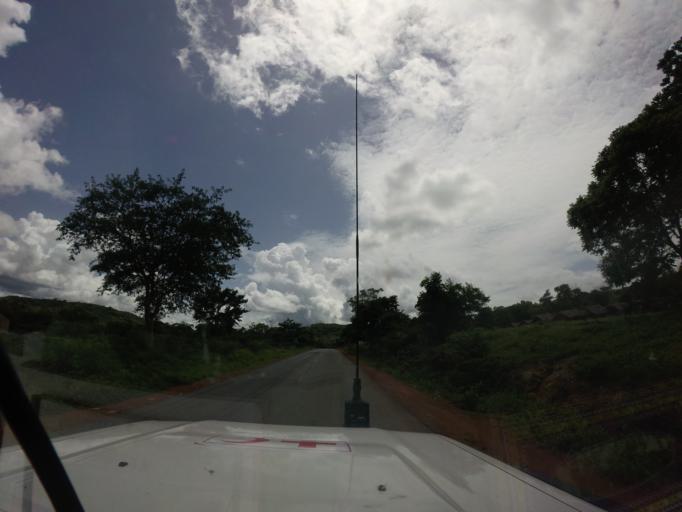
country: SL
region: Northern Province
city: Bindi
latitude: 10.1739
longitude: -11.2979
